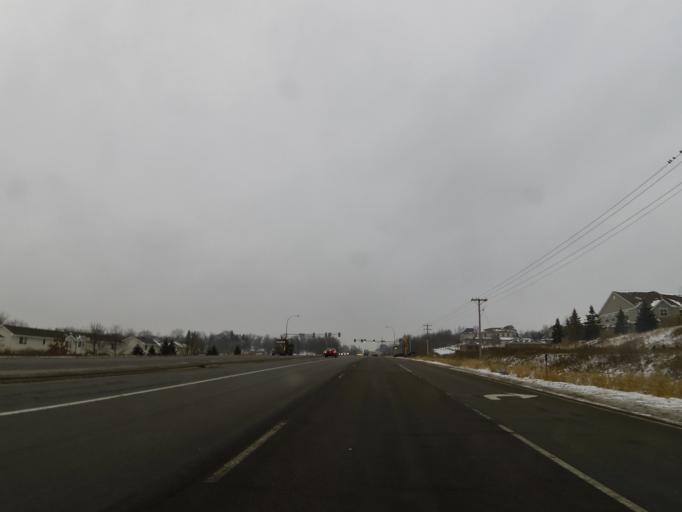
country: US
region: Minnesota
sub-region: Scott County
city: Savage
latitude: 44.7624
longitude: -93.3798
